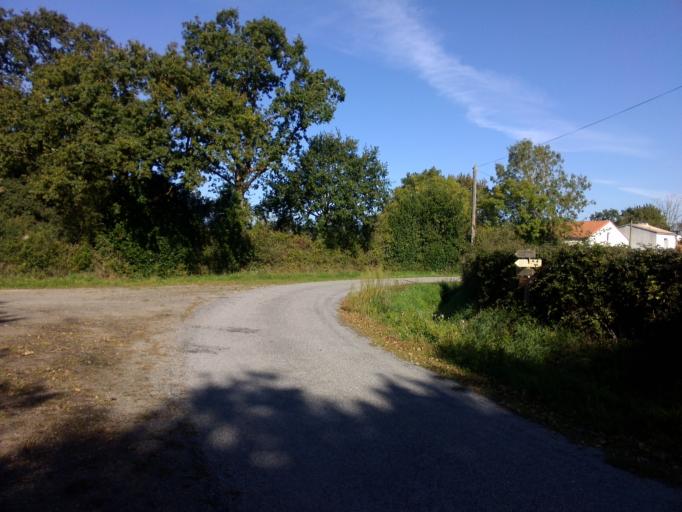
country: FR
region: Pays de la Loire
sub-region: Departement de la Loire-Atlantique
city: Chemere
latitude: 47.1087
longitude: -1.9213
